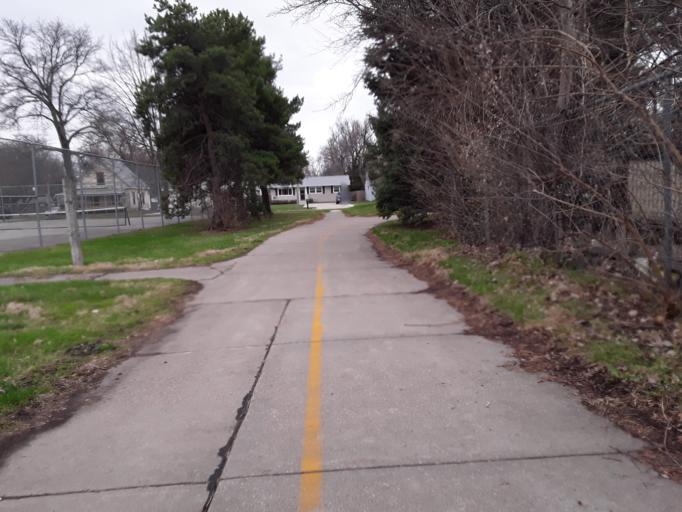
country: US
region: Nebraska
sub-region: Lancaster County
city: Lincoln
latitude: 40.8419
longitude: -96.6660
